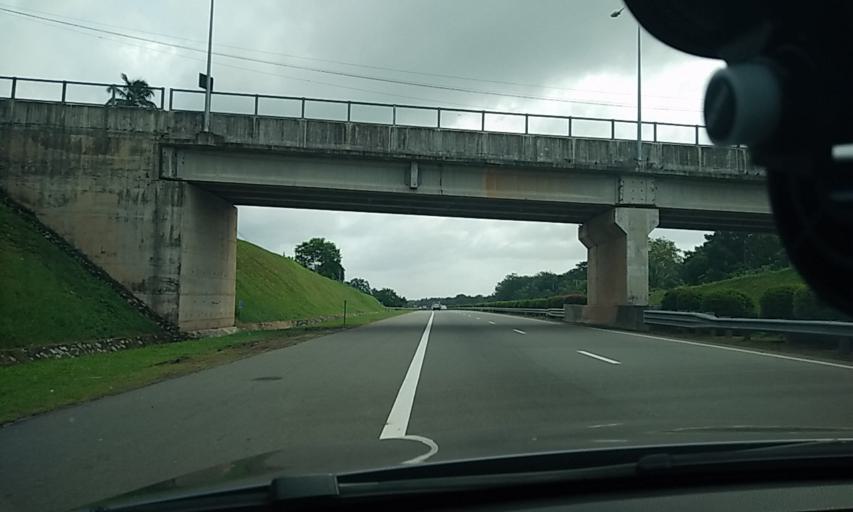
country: LK
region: Western
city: Homagama
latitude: 6.8634
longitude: 79.9781
